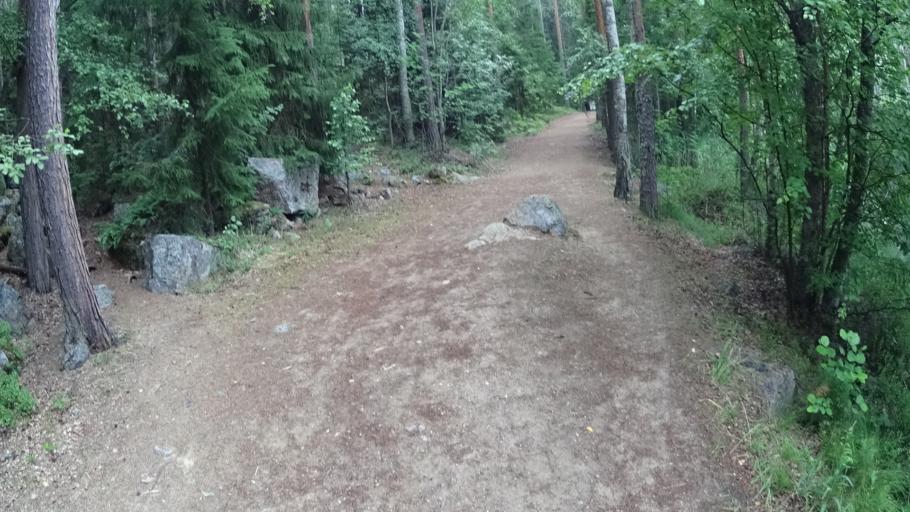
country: FI
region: Southern Savonia
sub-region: Mikkeli
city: Maentyharju
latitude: 61.1846
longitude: 26.8401
